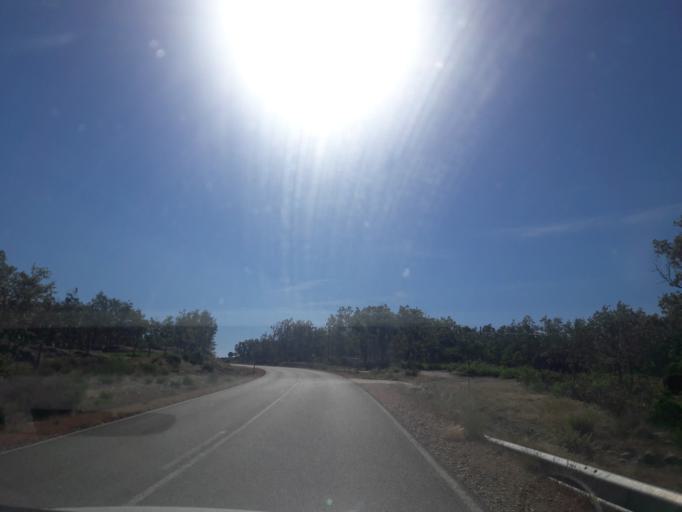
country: ES
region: Castille and Leon
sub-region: Provincia de Salamanca
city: Lagunilla
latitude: 40.3258
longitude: -5.9398
